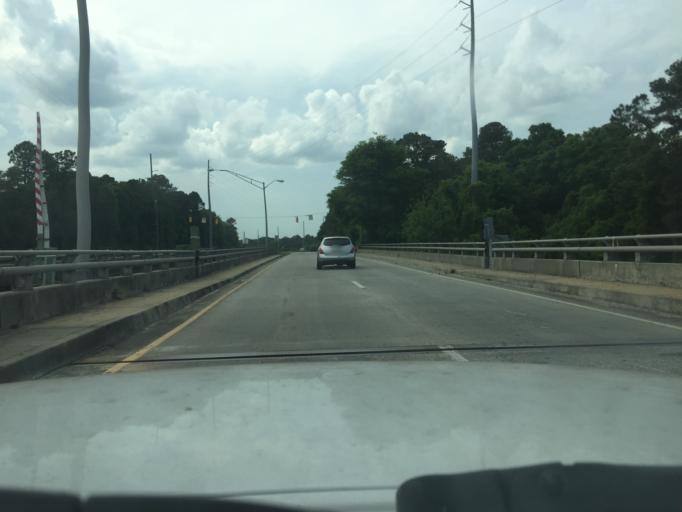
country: US
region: Georgia
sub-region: Chatham County
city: Thunderbolt
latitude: 32.0622
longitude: -81.0298
